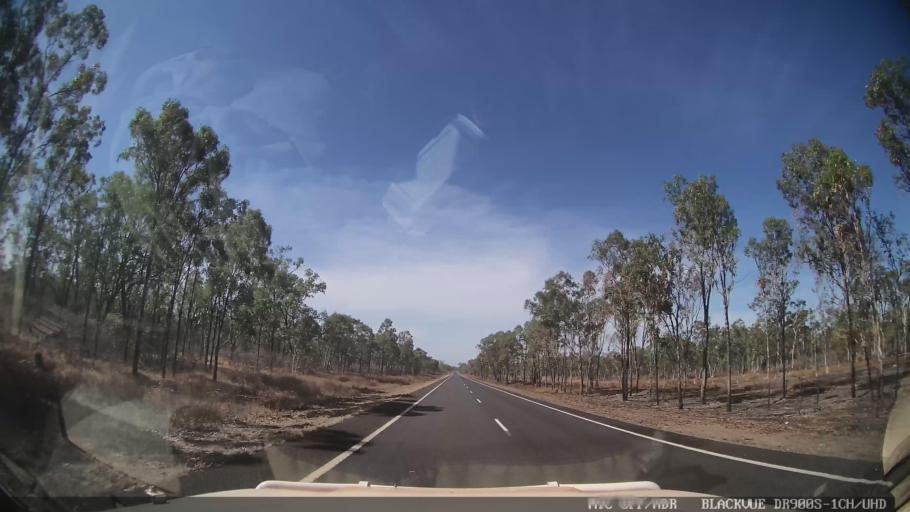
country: AU
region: Queensland
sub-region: Cook
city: Cooktown
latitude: -15.7859
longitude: 144.9538
